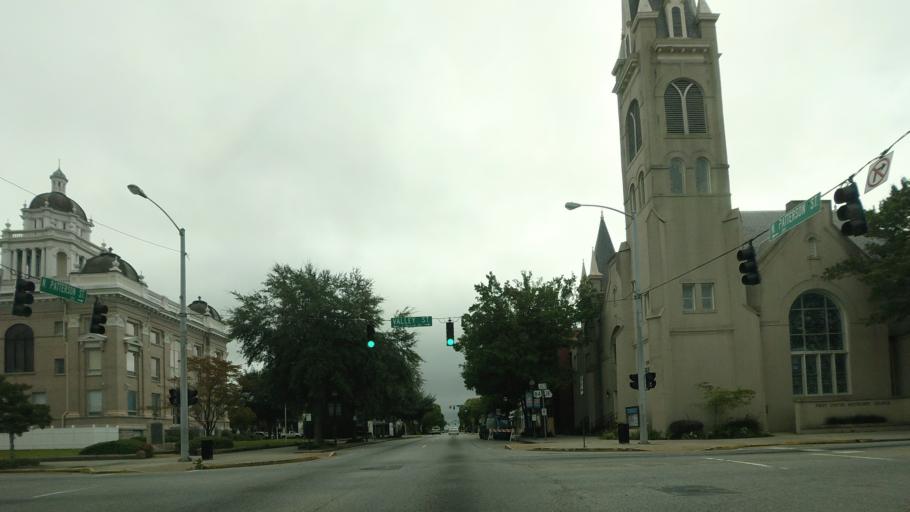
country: US
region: Georgia
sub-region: Lowndes County
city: Valdosta
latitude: 30.8328
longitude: -83.2799
